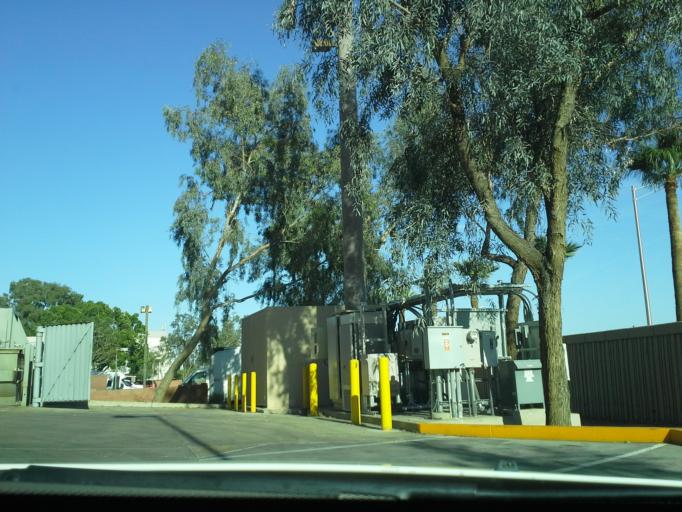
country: US
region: Arizona
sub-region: Maricopa County
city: Phoenix
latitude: 33.4631
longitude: -112.0641
